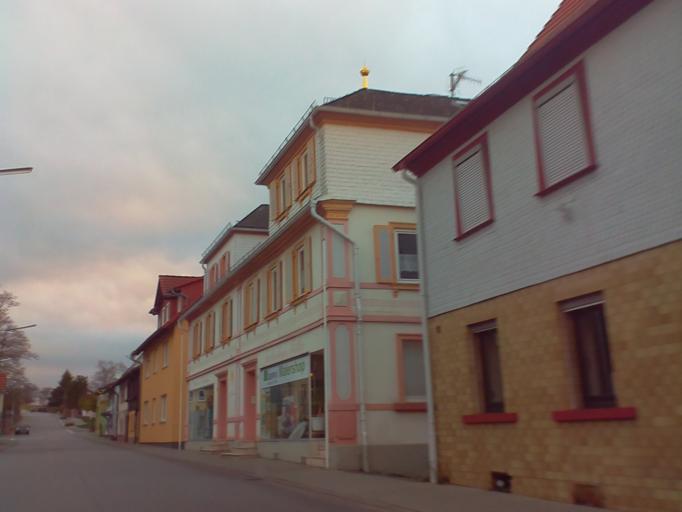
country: DE
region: Hesse
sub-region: Regierungsbezirk Darmstadt
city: Beerfelden
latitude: 49.5690
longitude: 8.9737
